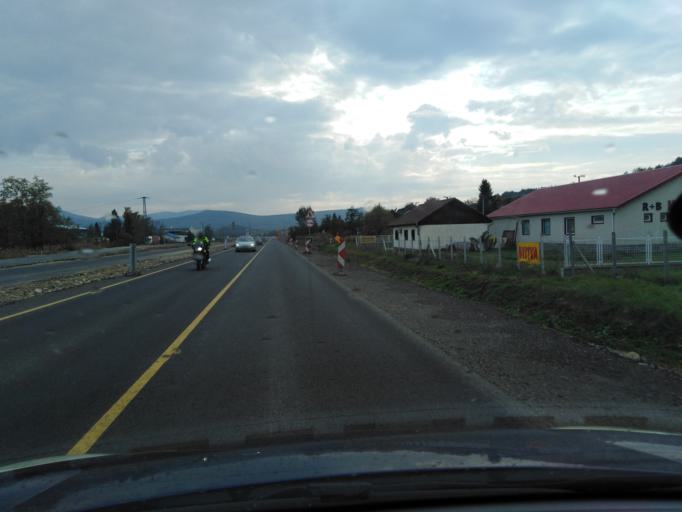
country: HU
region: Nograd
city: Batonyterenye
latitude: 47.9988
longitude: 19.8207
